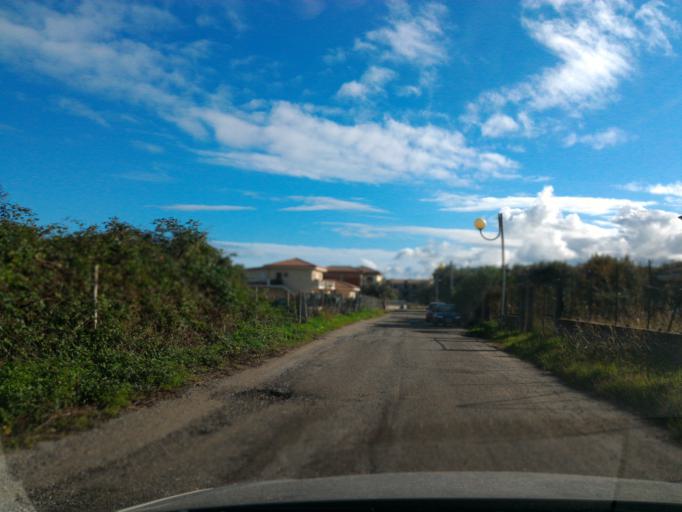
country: IT
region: Calabria
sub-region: Provincia di Crotone
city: Torretta
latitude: 39.4584
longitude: 17.0335
